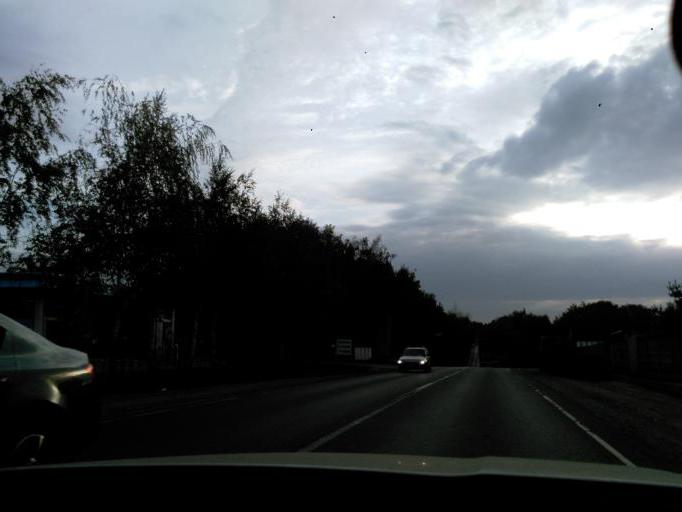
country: RU
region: Moskovskaya
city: Sheremet'yevskiy
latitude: 55.9721
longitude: 37.4515
